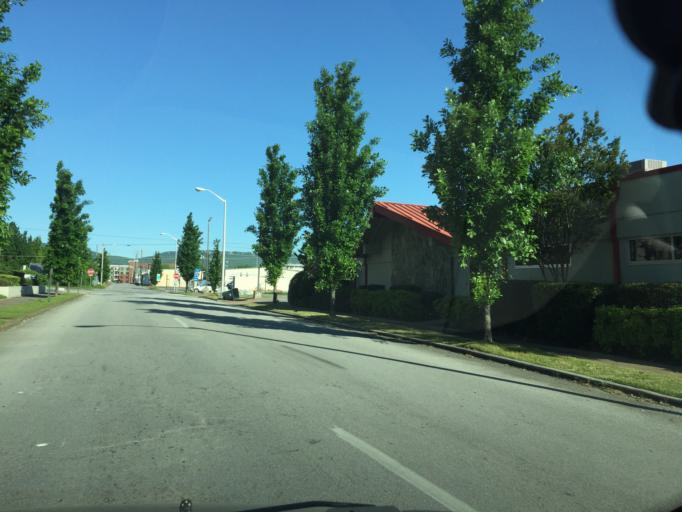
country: US
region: Tennessee
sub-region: Hamilton County
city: Chattanooga
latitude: 35.0315
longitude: -85.3111
